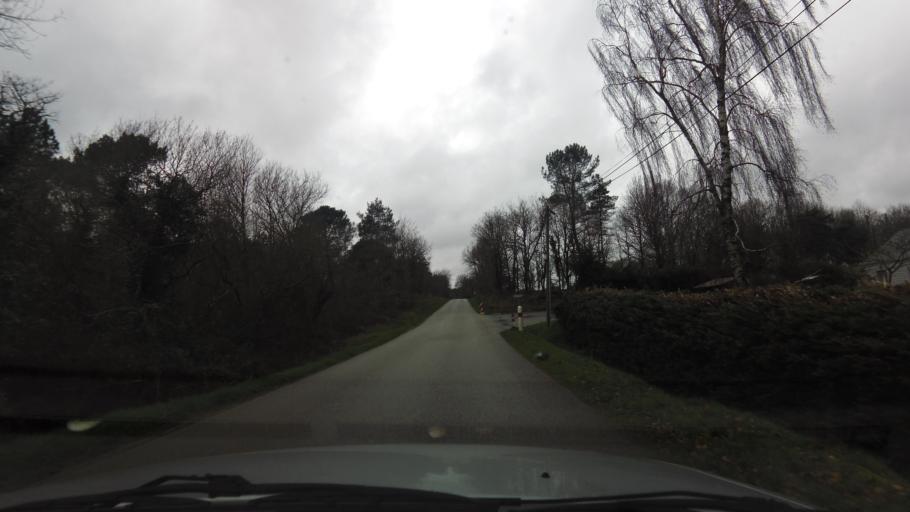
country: FR
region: Brittany
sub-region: Departement du Morbihan
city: Serent
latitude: 47.7776
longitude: -2.5383
